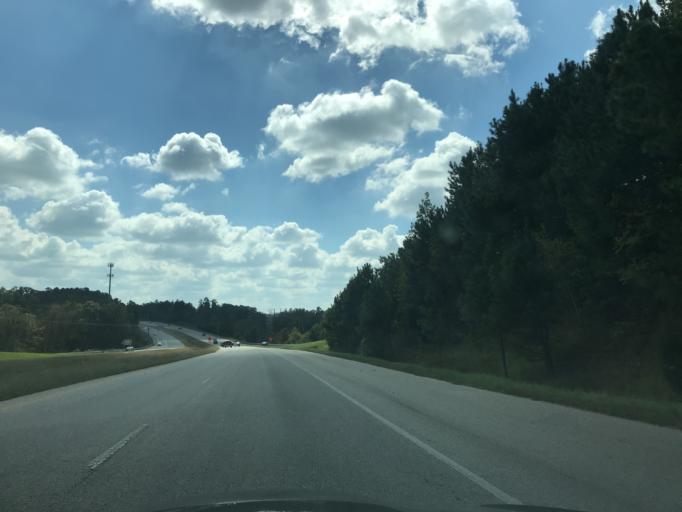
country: US
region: North Carolina
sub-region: Wake County
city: Wake Forest
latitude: 35.9648
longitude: -78.5422
